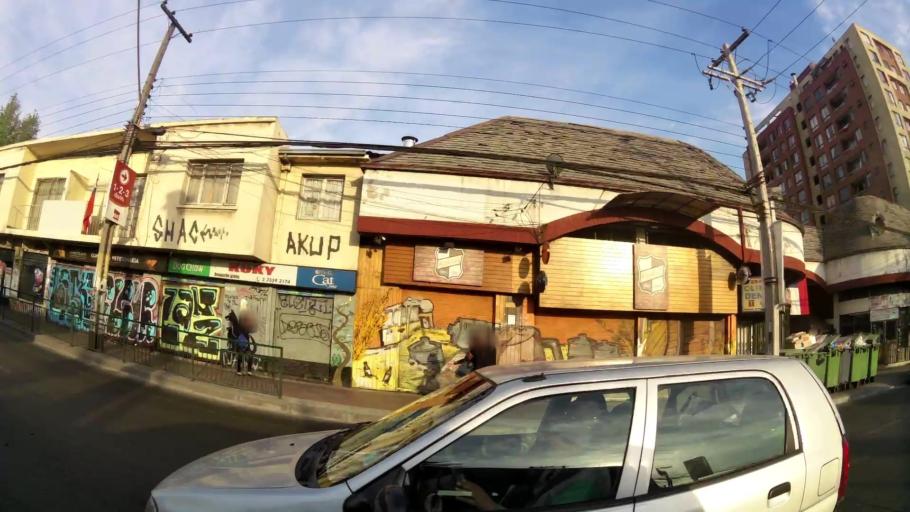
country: CL
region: Santiago Metropolitan
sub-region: Provincia de Santiago
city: Santiago
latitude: -33.5104
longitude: -70.6570
